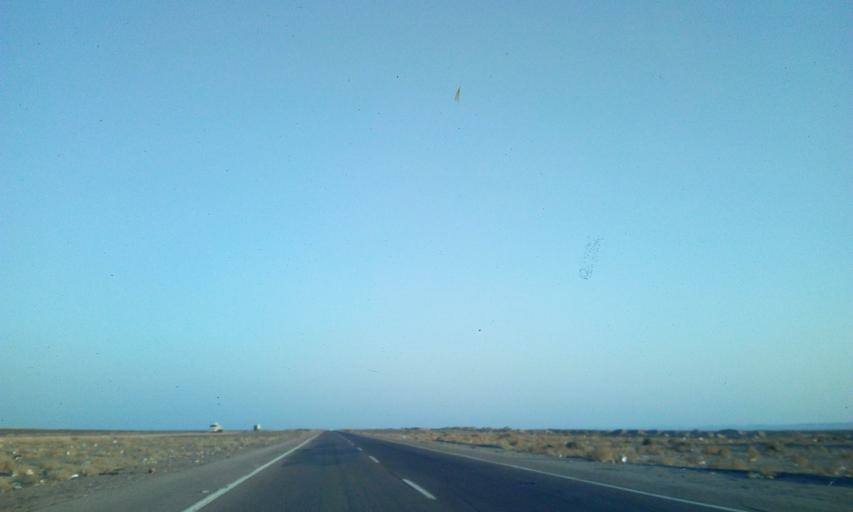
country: EG
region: South Sinai
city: Tor
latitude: 27.9311
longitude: 33.3824
